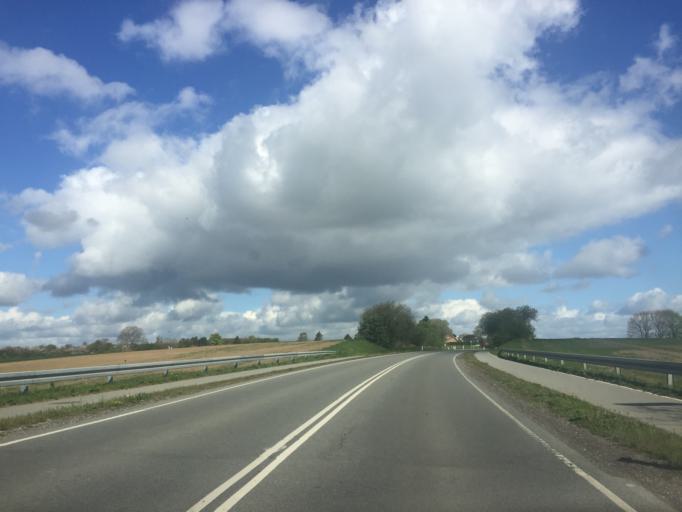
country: DK
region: Zealand
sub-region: Stevns Kommune
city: Stroby Egede
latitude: 55.4024
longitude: 12.2353
